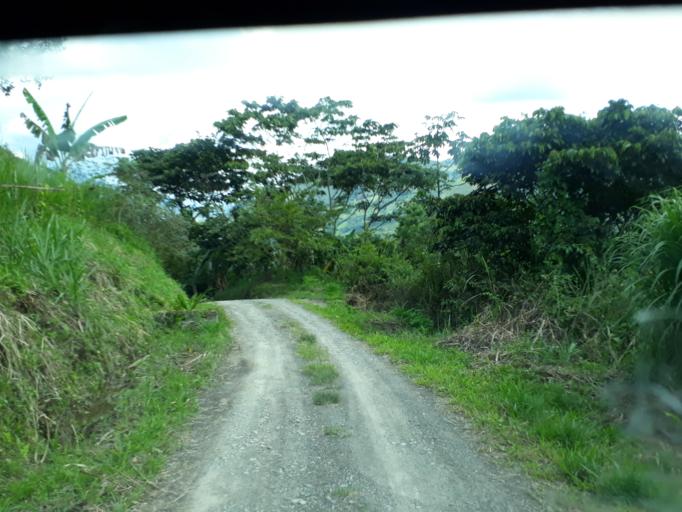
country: CO
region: Cundinamarca
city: Topaipi
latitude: 5.2774
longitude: -74.3532
